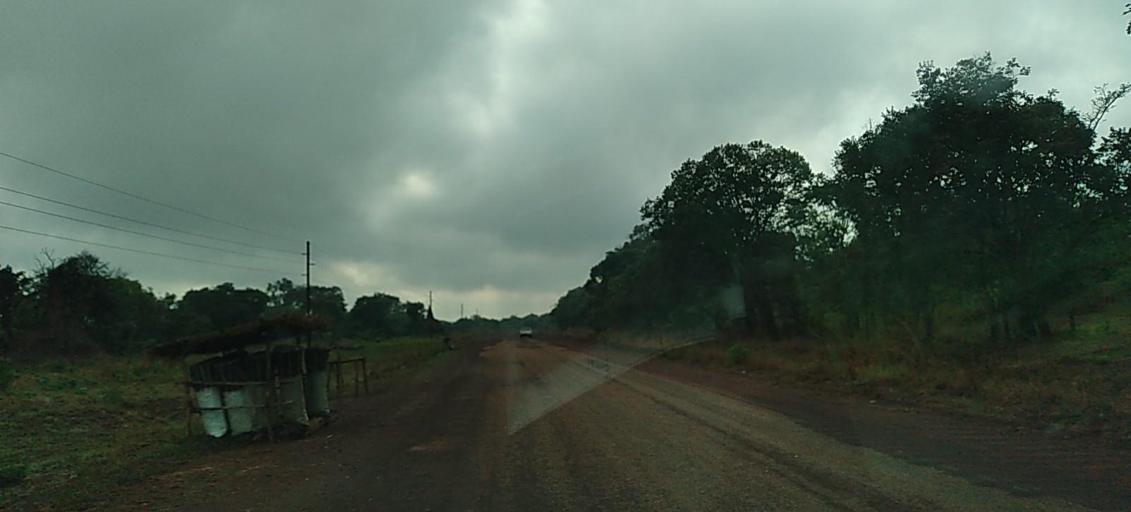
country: ZM
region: North-Western
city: Mwinilunga
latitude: -11.7252
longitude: 24.5723
